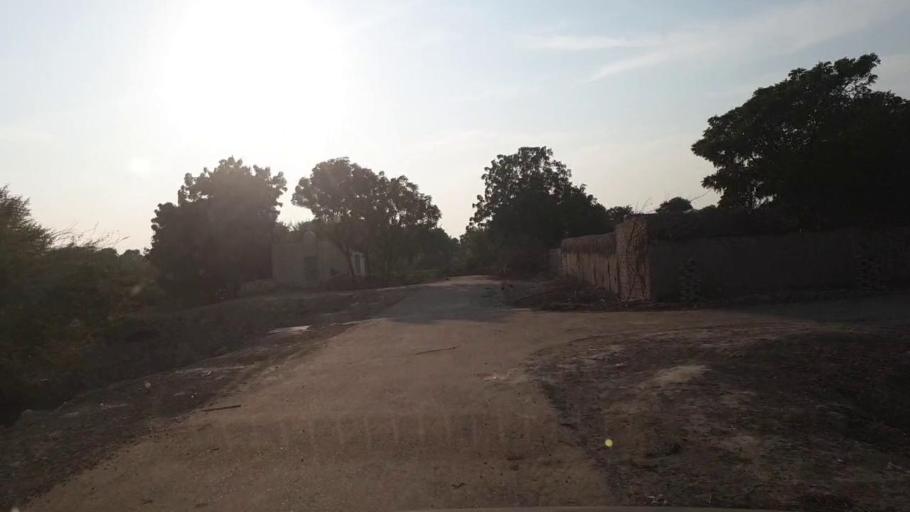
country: PK
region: Sindh
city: Shahpur Chakar
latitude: 26.1513
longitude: 68.6355
